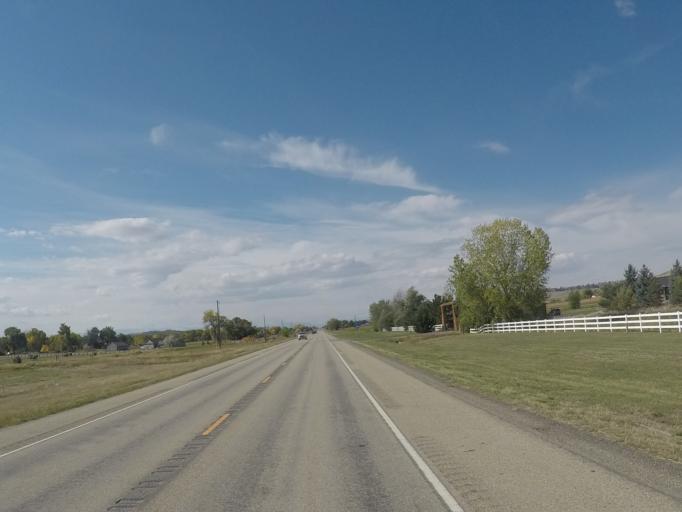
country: US
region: Montana
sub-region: Yellowstone County
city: Laurel
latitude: 45.5157
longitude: -108.8827
